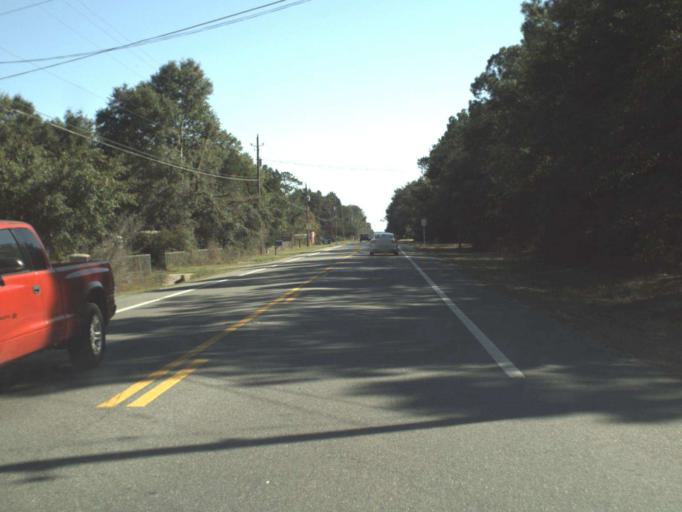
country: US
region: Florida
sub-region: Okaloosa County
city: Crestview
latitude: 30.7618
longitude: -86.6618
